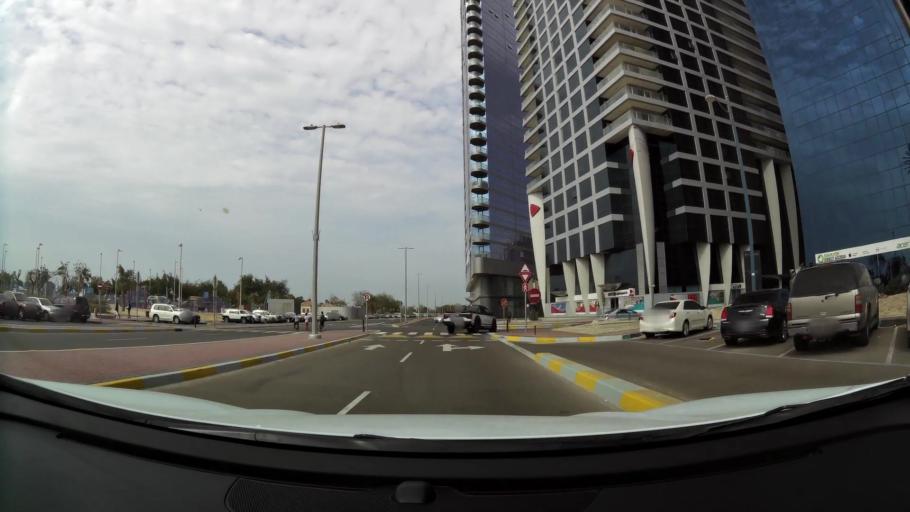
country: AE
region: Abu Dhabi
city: Abu Dhabi
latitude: 24.4822
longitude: 54.3495
